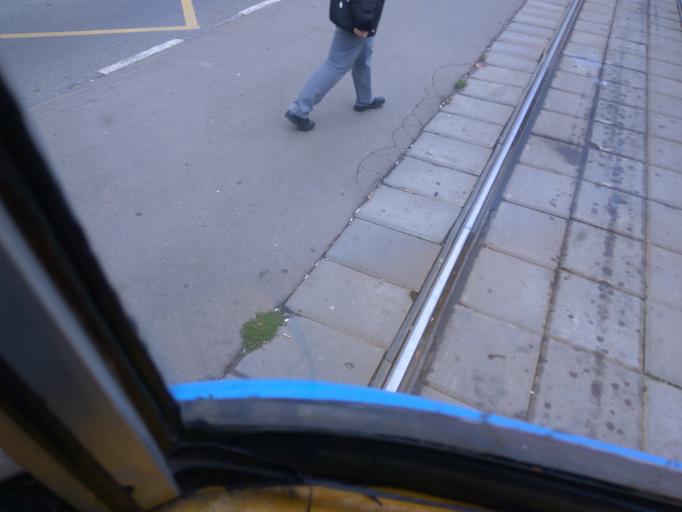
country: RU
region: Moscow
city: Kotlovka
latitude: 55.6562
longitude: 37.6053
